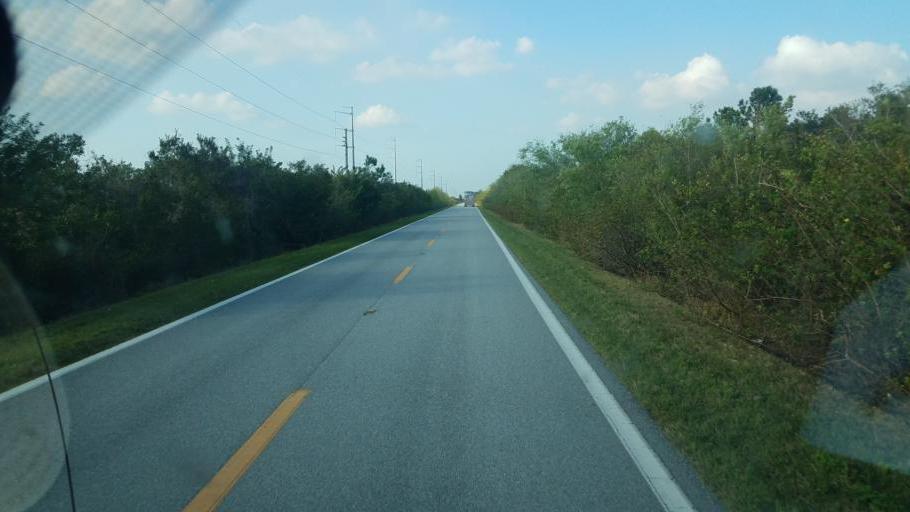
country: US
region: Florida
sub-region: Hardee County
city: Bowling Green
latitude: 27.6693
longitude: -81.9530
